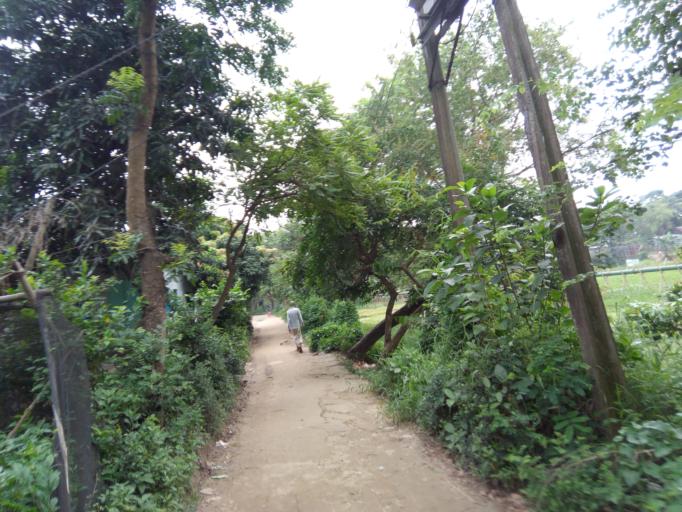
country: BD
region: Dhaka
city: Paltan
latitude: 23.7574
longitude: 90.4556
